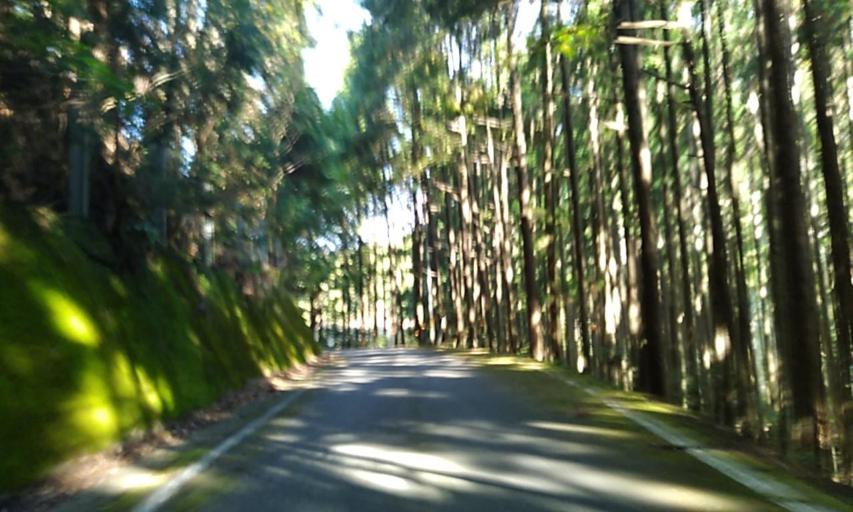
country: JP
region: Wakayama
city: Shingu
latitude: 33.9144
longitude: 135.9903
